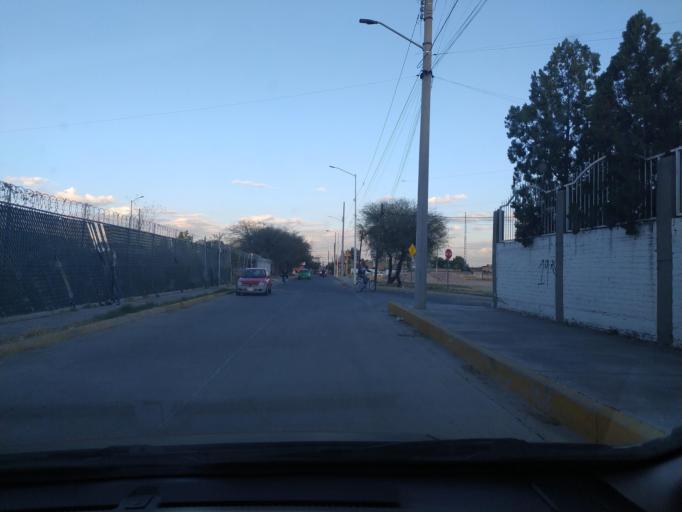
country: LA
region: Oudomxai
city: Muang La
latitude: 21.0137
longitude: 101.8711
